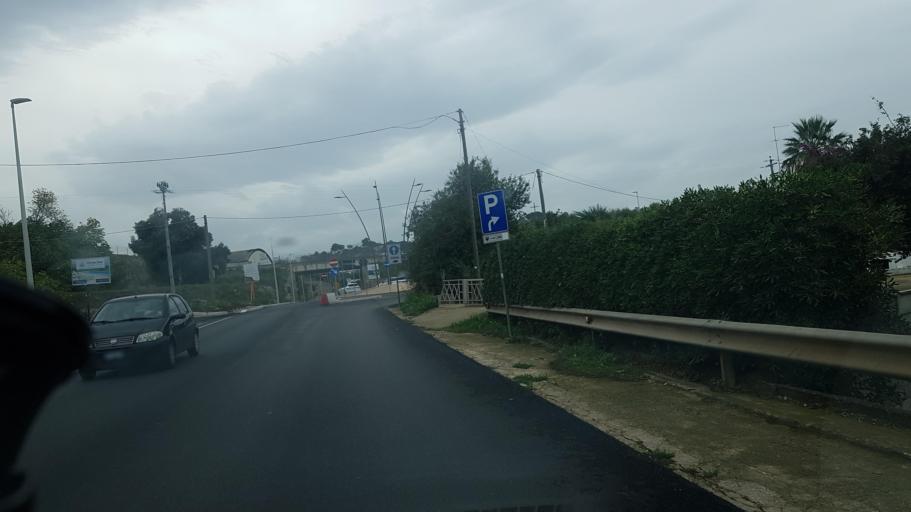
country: IT
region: Apulia
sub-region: Provincia di Brindisi
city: Ostuni
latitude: 40.7373
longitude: 17.5738
